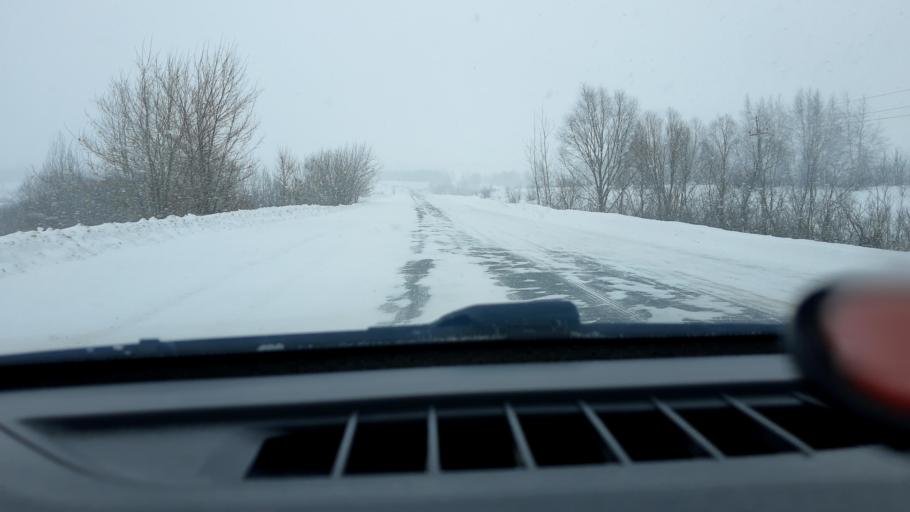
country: RU
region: Nizjnij Novgorod
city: Bol'shoye Murashkino
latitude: 55.7656
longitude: 44.7546
